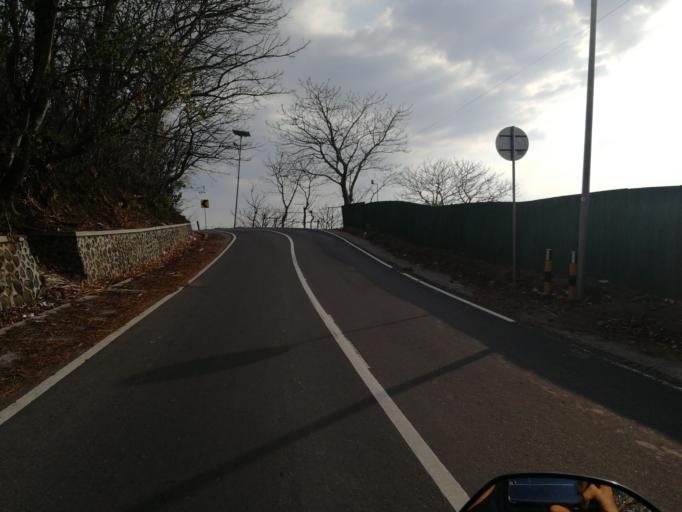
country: ID
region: West Nusa Tenggara
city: Karangsubagan
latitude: -8.4469
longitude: 116.0333
